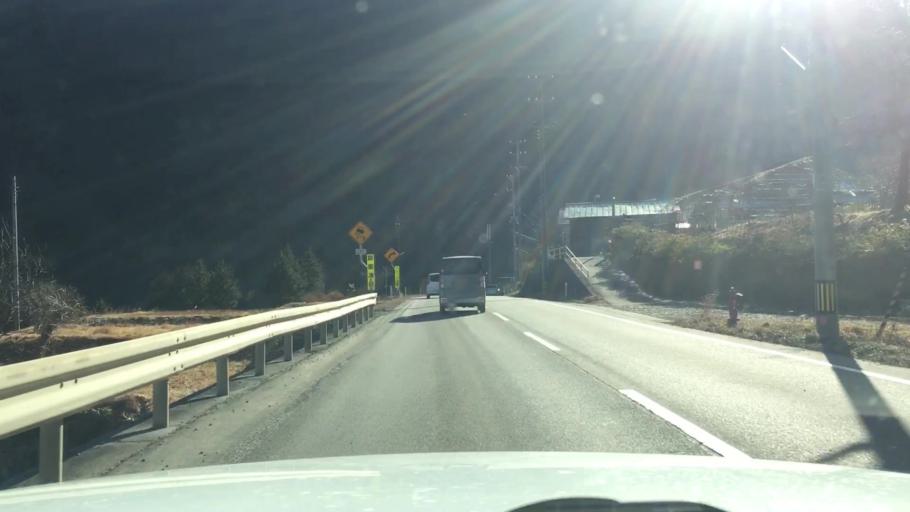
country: JP
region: Iwate
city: Miyako
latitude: 39.6078
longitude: 141.7869
